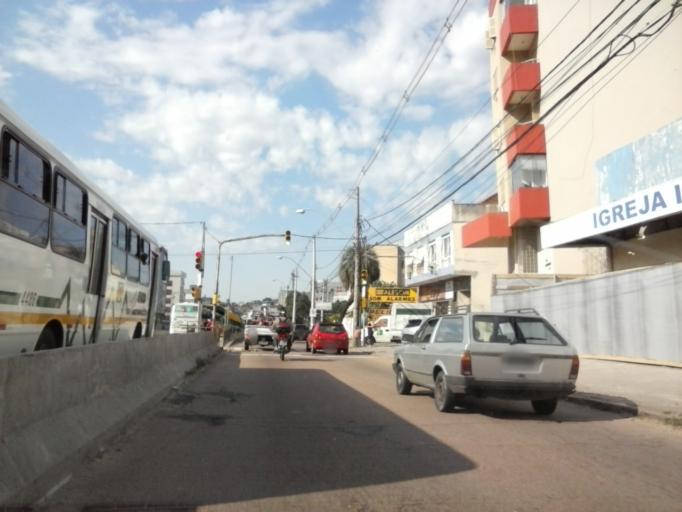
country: BR
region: Rio Grande do Sul
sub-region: Porto Alegre
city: Porto Alegre
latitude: -30.0408
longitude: -51.1680
